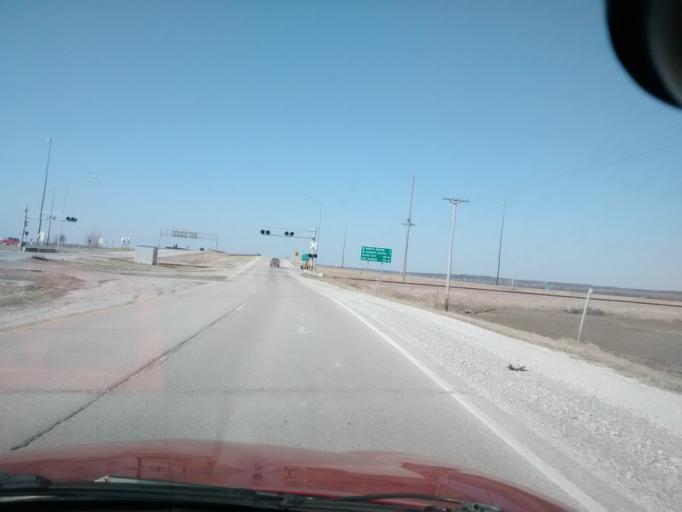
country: US
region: Iowa
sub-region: Pottawattamie County
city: Carter Lake
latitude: 41.3557
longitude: -95.8968
